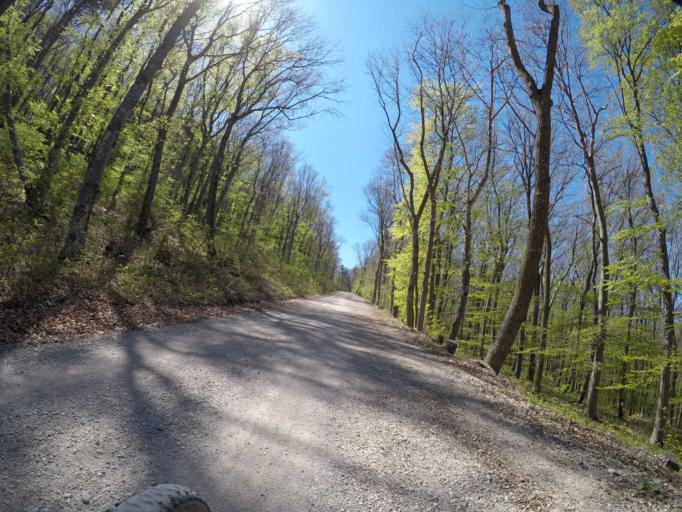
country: AT
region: Lower Austria
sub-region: Politischer Bezirk Modling
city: Hinterbruehl
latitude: 48.0580
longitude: 16.2478
